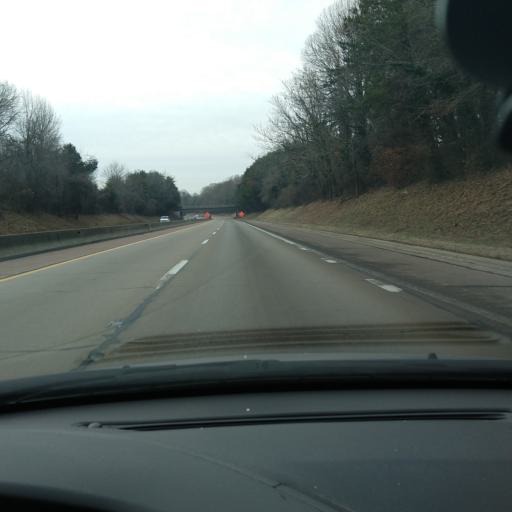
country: US
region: North Carolina
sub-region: Forsyth County
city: Winston-Salem
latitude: 36.0439
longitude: -80.2385
